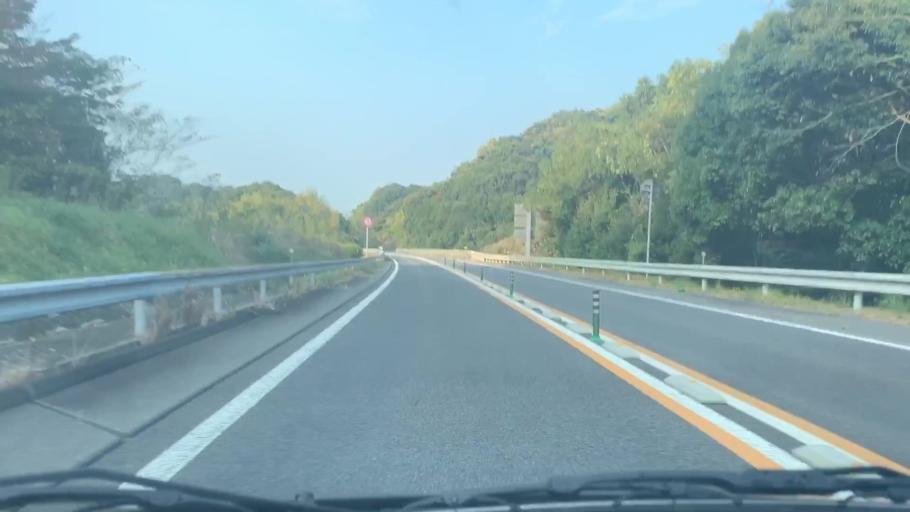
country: JP
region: Nagasaki
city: Sasebo
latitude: 33.1513
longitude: 129.7978
